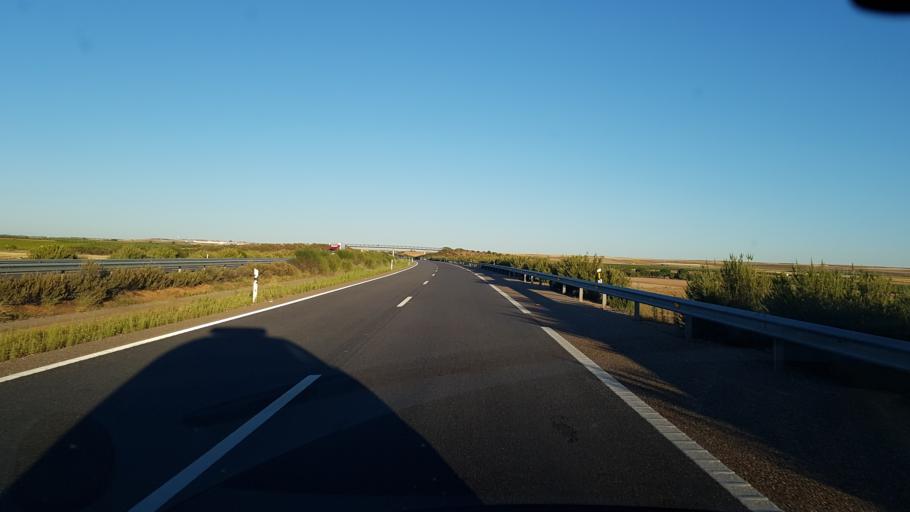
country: ES
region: Castille and Leon
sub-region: Provincia de Zamora
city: Morales de Toro
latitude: 41.5453
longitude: -5.3096
